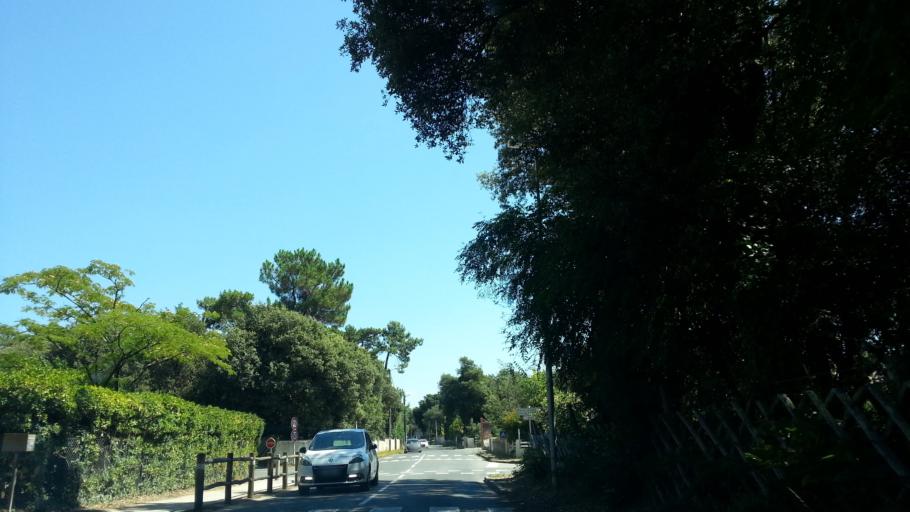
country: FR
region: Poitou-Charentes
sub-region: Departement de la Charente-Maritime
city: Dolus-d'Oleron
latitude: 45.8844
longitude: -1.2580
